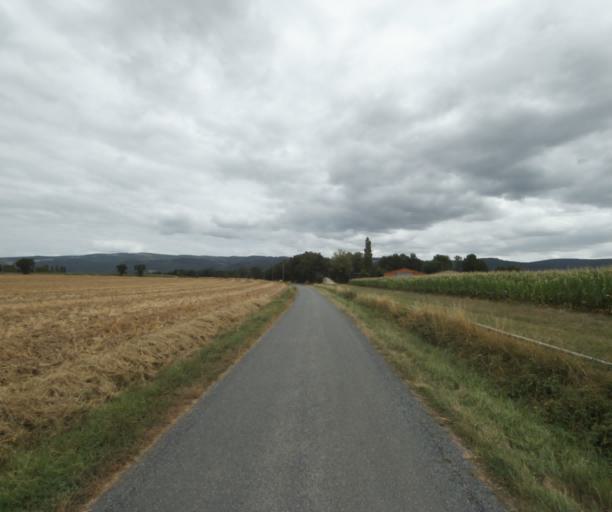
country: FR
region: Midi-Pyrenees
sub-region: Departement du Tarn
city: Soreze
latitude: 43.4820
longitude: 2.0610
